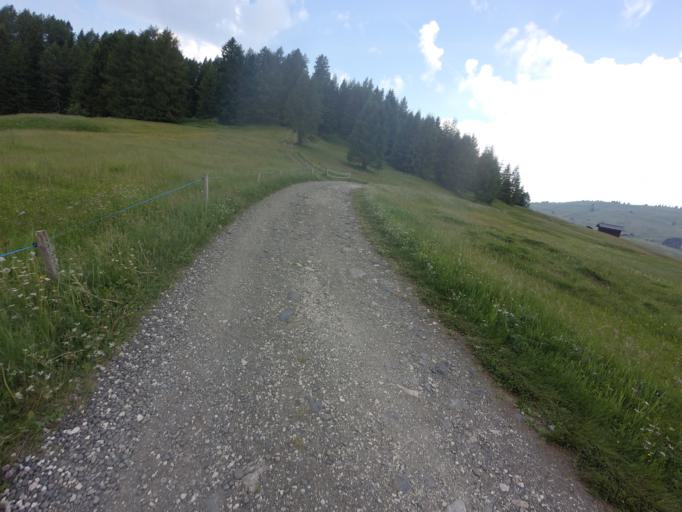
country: IT
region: Trentino-Alto Adige
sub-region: Bolzano
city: Ortisei
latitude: 46.5439
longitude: 11.6643
